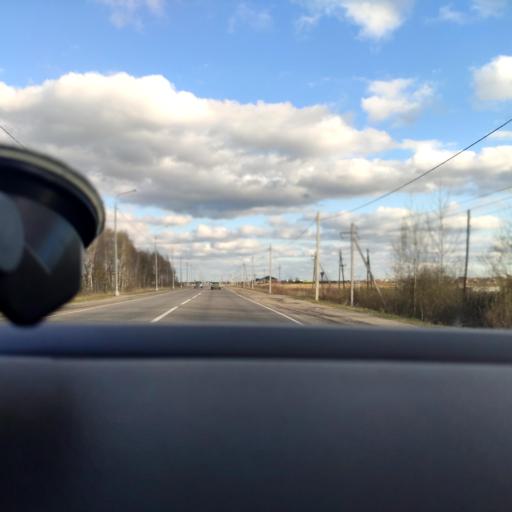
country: RU
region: Moskovskaya
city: Yegor'yevsk
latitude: 55.4078
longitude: 39.0531
